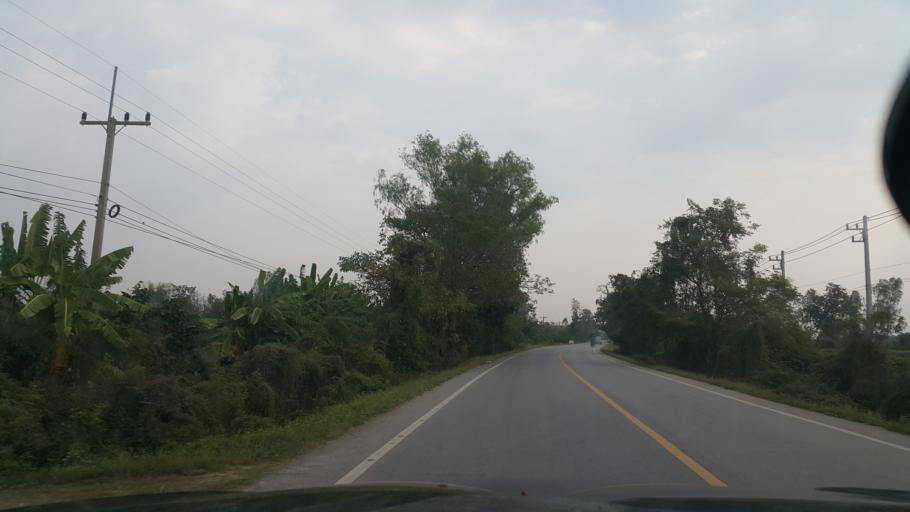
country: TH
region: Sukhothai
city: Si Samrong
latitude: 17.1713
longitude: 99.7247
